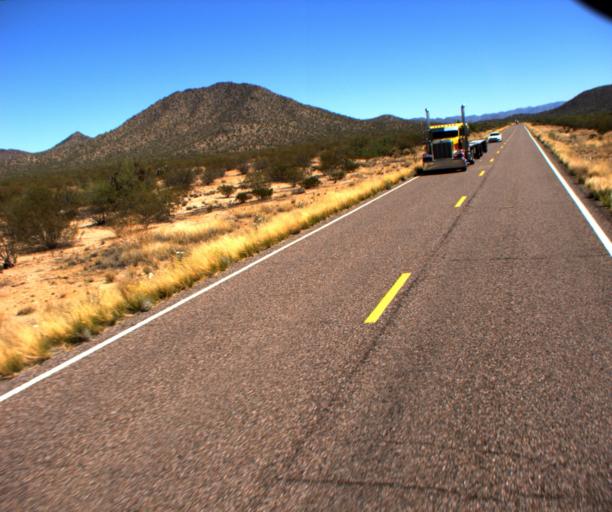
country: US
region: Arizona
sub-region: Yavapai County
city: Congress
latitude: 34.0875
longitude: -113.0117
